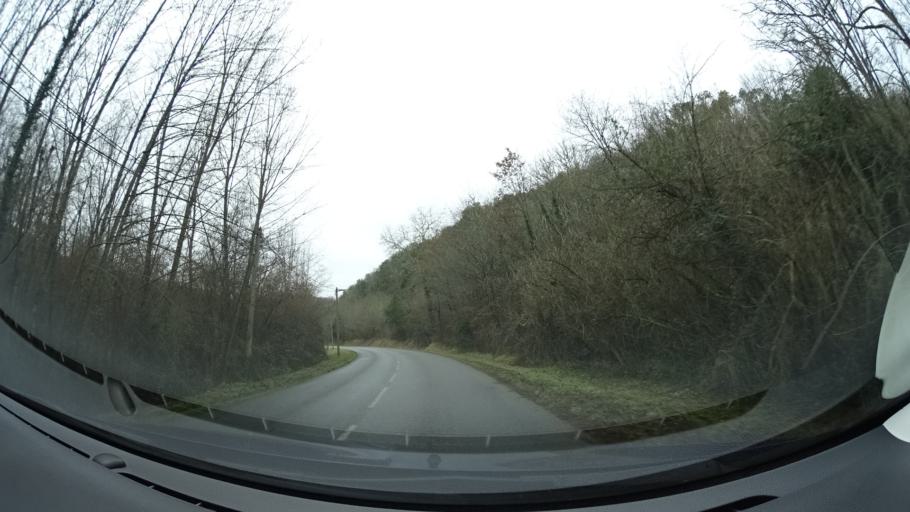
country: FR
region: Aquitaine
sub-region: Departement de la Dordogne
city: Saint-Cyprien
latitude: 44.8844
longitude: 1.0870
